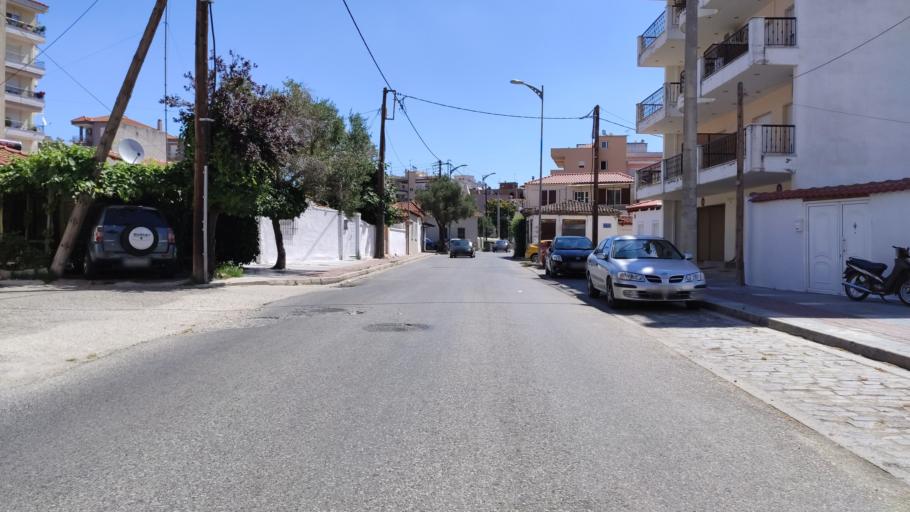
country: GR
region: East Macedonia and Thrace
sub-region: Nomos Rodopis
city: Komotini
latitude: 41.1238
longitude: 25.4076
